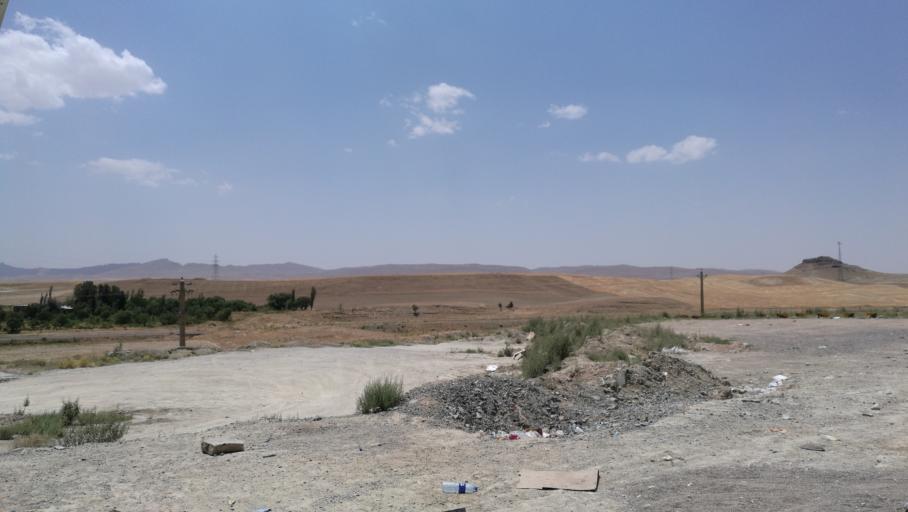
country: IR
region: Markazi
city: Komijan
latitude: 35.1129
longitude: 49.6122
